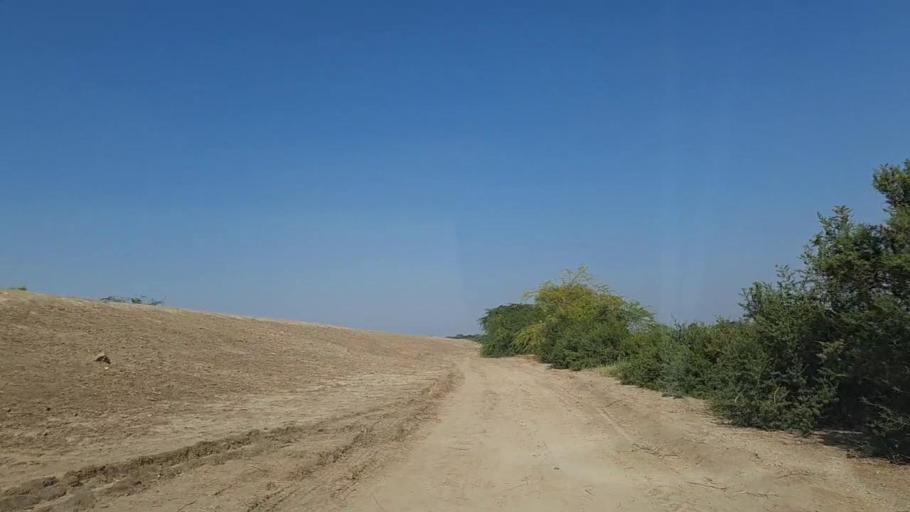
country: PK
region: Sindh
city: Chuhar Jamali
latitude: 24.4847
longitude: 68.0147
